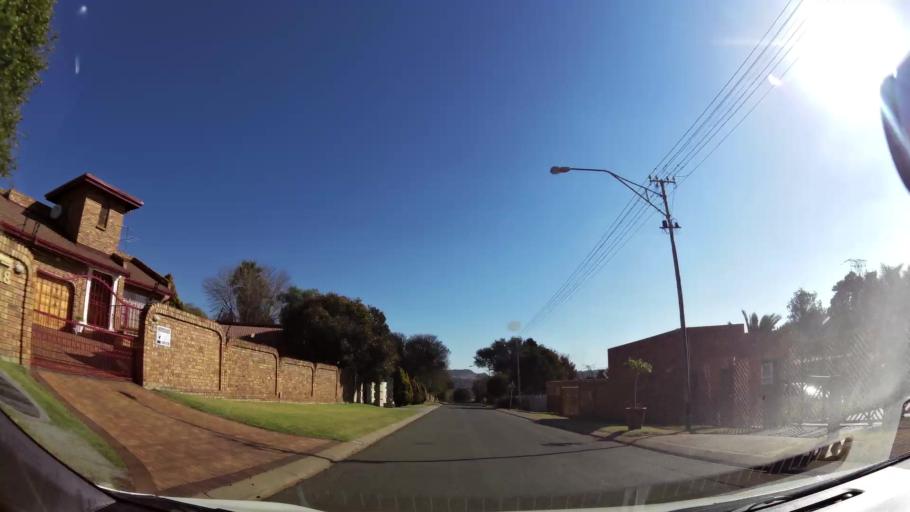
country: ZA
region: Gauteng
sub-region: City of Johannesburg Metropolitan Municipality
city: Johannesburg
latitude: -26.2774
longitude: 28.0190
